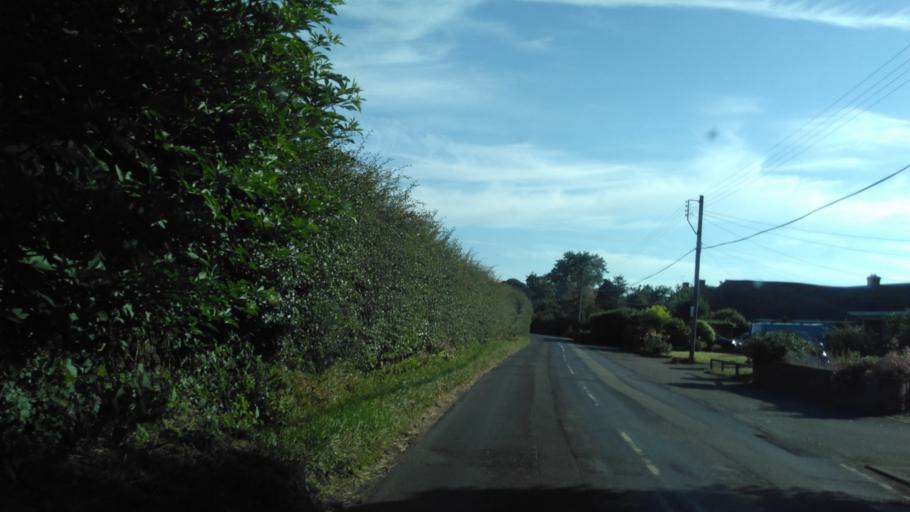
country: GB
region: England
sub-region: Kent
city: Dunkirk
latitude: 51.3235
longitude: 0.9424
